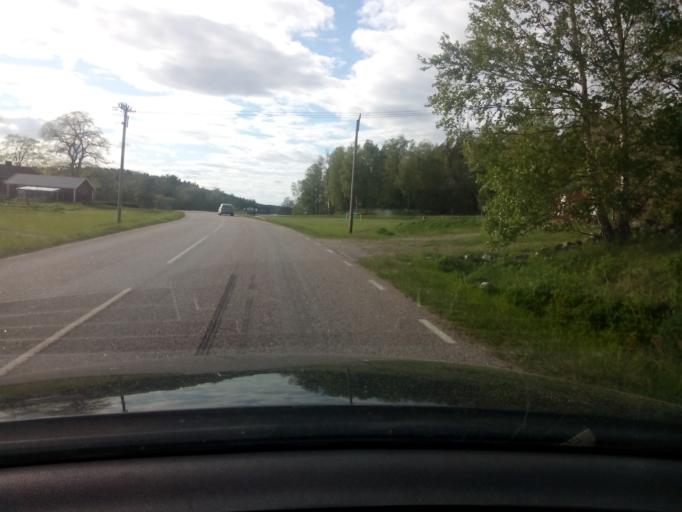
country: SE
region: Soedermanland
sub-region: Nykopings Kommun
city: Stigtomta
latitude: 58.9493
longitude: 16.8889
